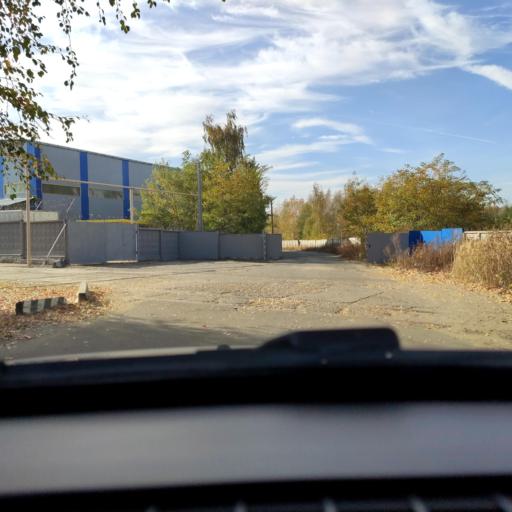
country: RU
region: Voronezj
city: Podgornoye
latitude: 51.8018
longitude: 39.1972
